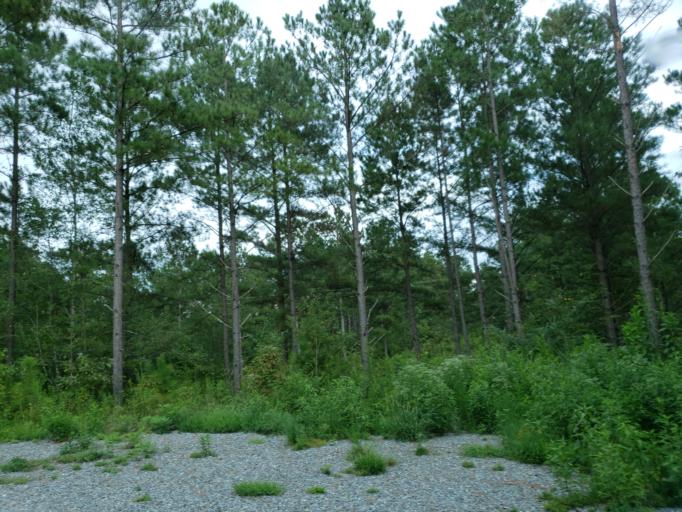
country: US
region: Georgia
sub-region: Pickens County
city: Jasper
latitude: 34.5383
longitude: -84.5241
